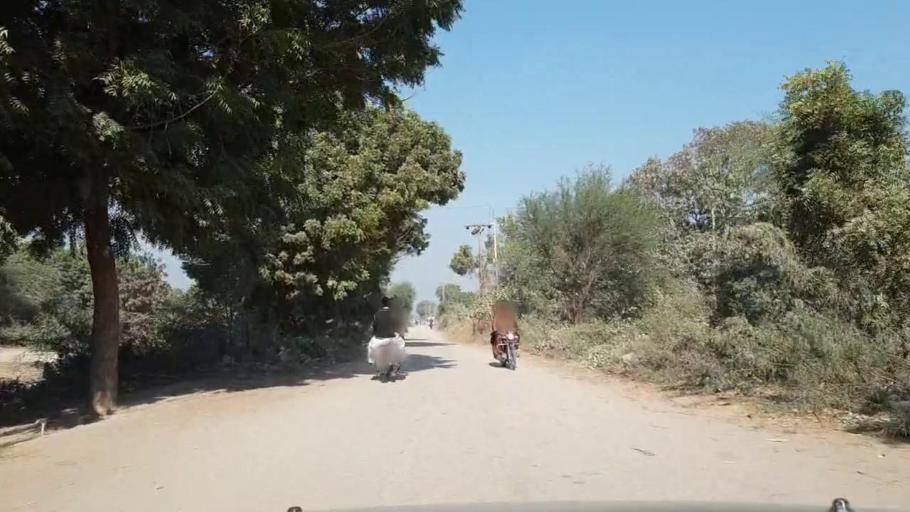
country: PK
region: Sindh
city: Matiari
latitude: 25.6065
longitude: 68.5977
